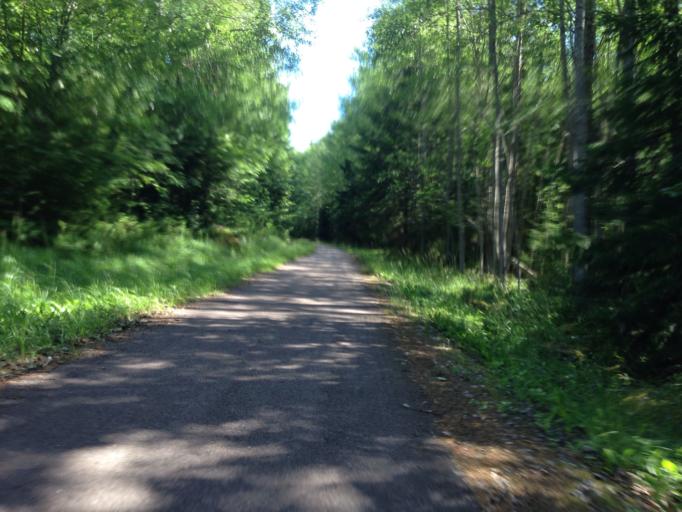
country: SE
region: Dalarna
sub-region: Ludvika Kommun
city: Grangesberg
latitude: 60.2113
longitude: 15.0492
